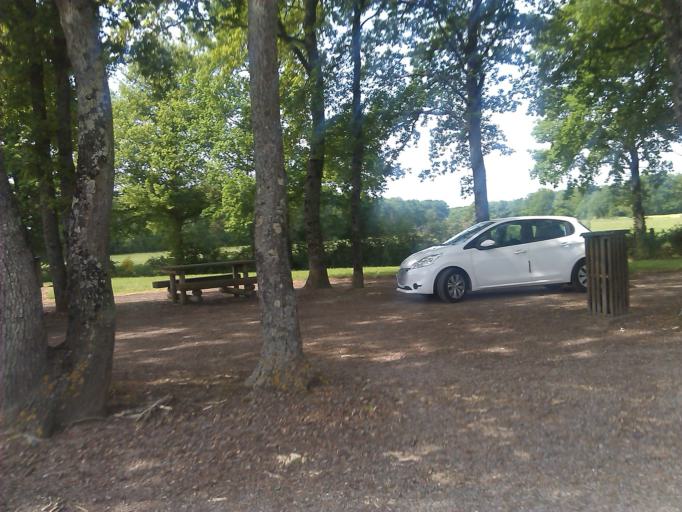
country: FR
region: Centre
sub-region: Departement de l'Indre
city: La Chatre
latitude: 46.5564
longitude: 2.0738
